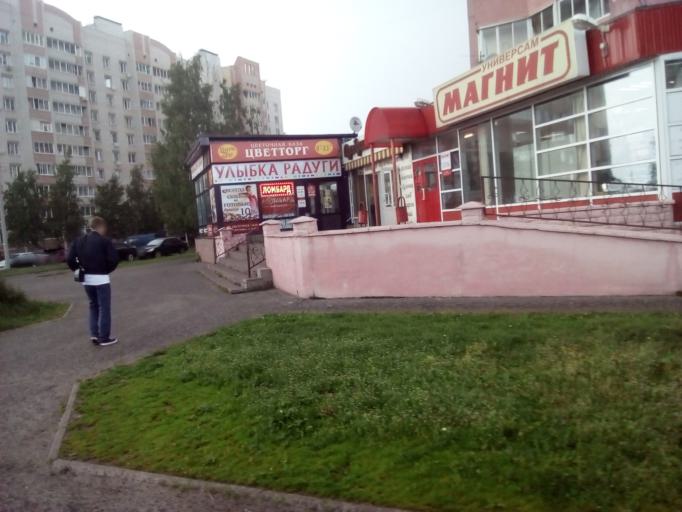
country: RU
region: Jaroslavl
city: Yaroslavl
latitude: 57.5838
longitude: 39.9095
